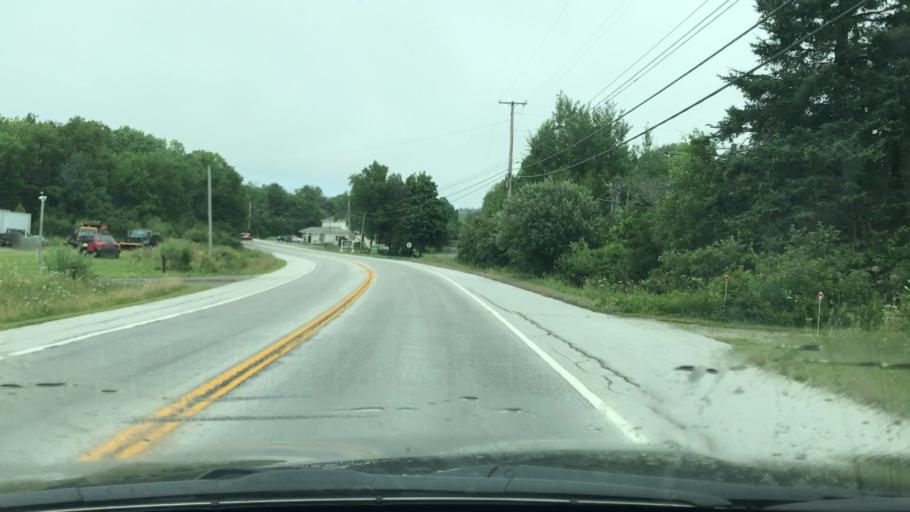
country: US
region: Maine
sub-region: Waldo County
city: Northport
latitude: 44.3322
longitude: -68.9571
